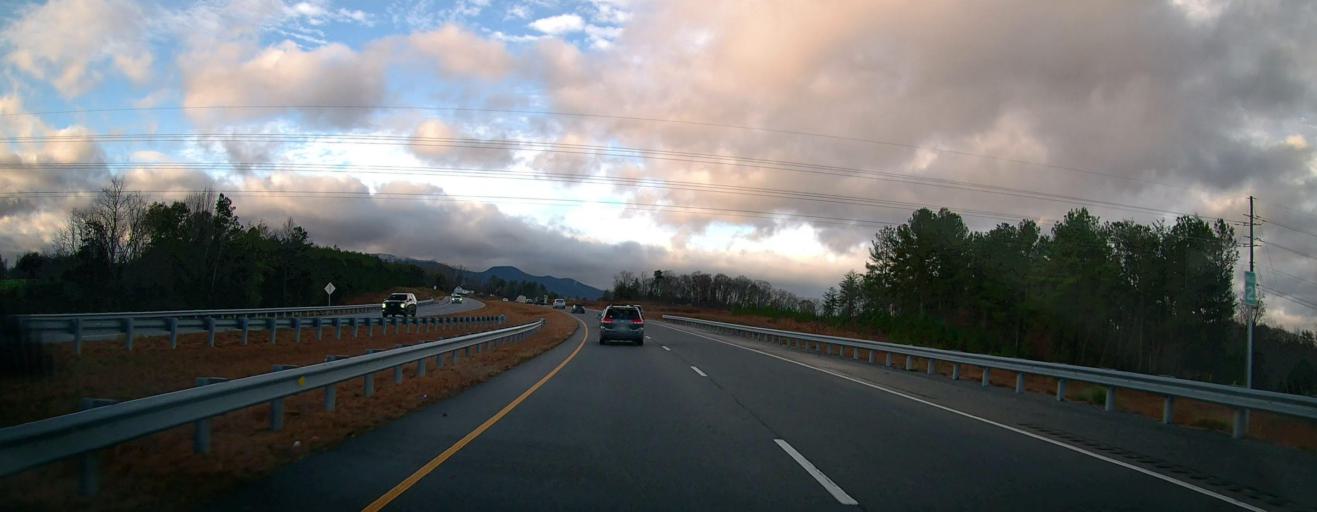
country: US
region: Georgia
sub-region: White County
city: Cleveland
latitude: 34.6002
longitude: -83.7806
